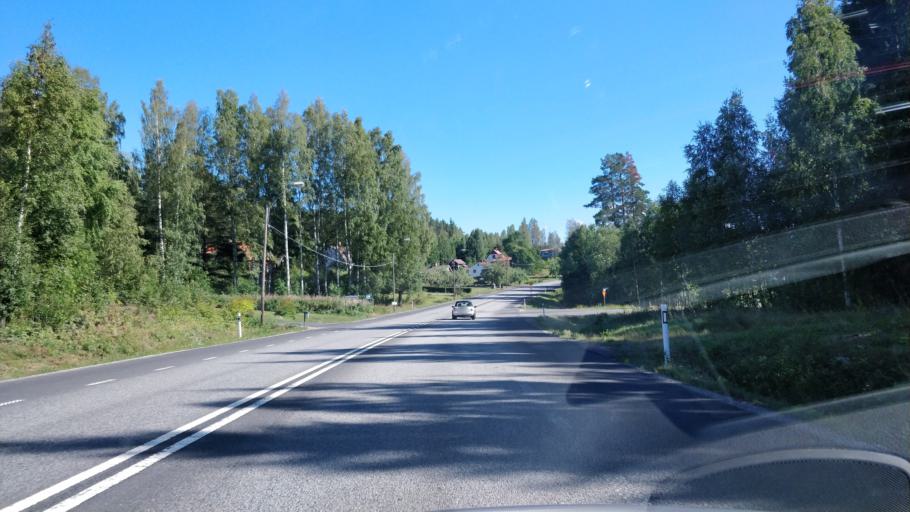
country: SE
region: Dalarna
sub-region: Faluns Kommun
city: Grycksbo
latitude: 60.6997
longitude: 15.4788
